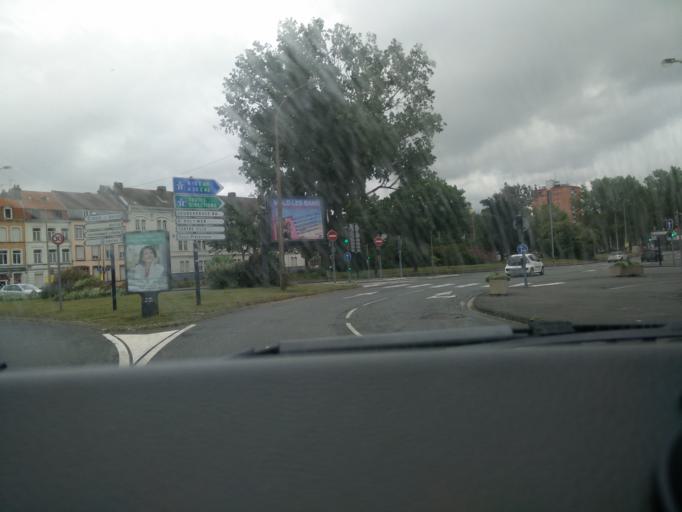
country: FR
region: Nord-Pas-de-Calais
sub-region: Departement du Nord
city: Dunkerque
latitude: 51.0320
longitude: 2.3708
